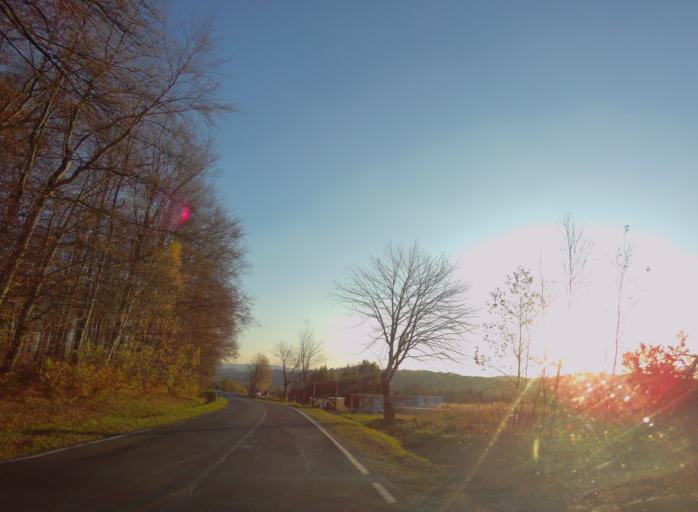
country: PL
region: Subcarpathian Voivodeship
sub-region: Powiat leski
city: Polanczyk
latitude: 49.3849
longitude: 22.4295
